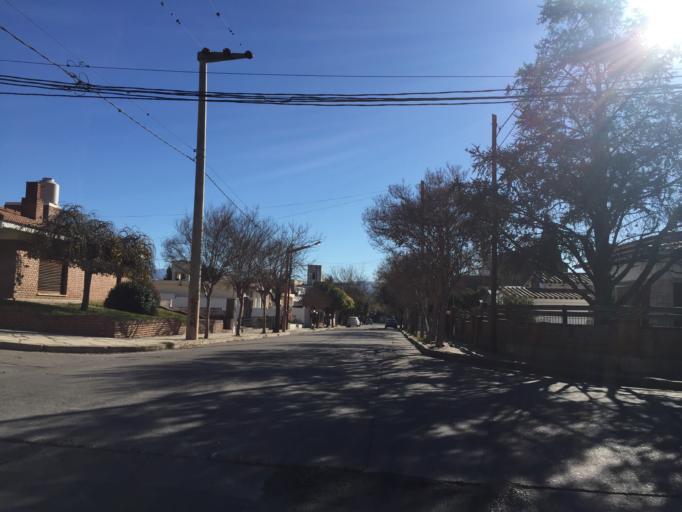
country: AR
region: Cordoba
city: Villa Carlos Paz
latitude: -31.4282
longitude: -64.4939
